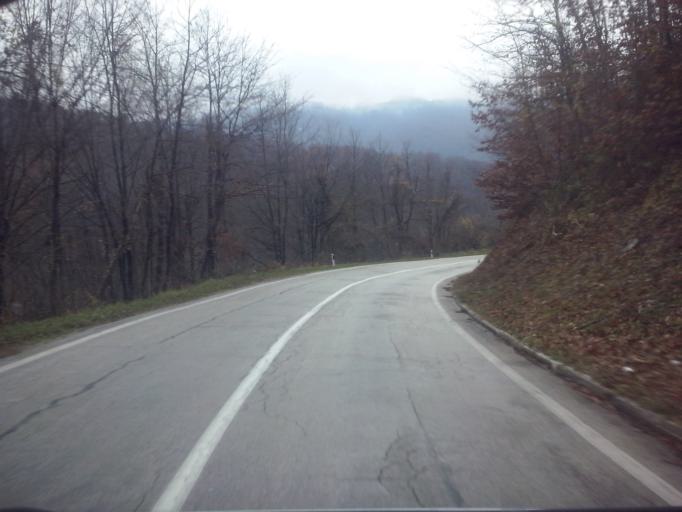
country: RS
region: Central Serbia
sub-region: Moravicki Okrug
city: Ivanjica
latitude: 43.5447
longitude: 20.2633
